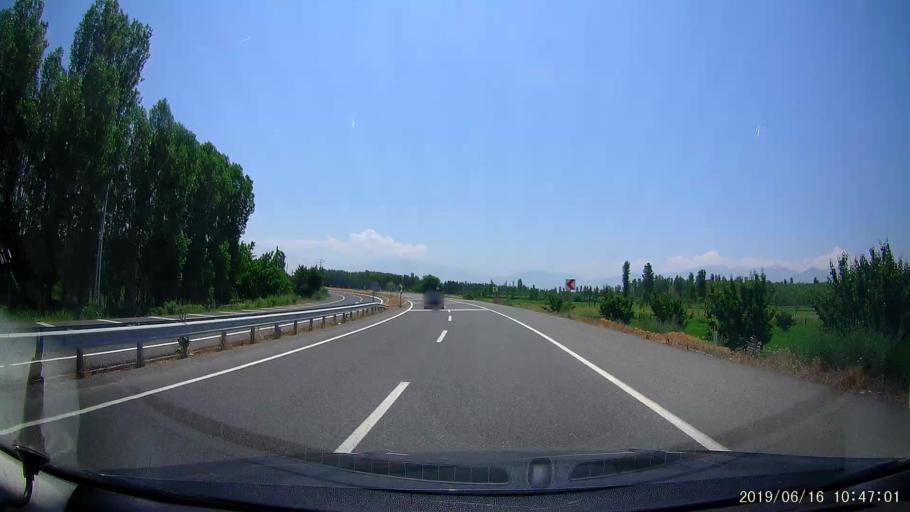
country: AM
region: Armavir
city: Shenavan
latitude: 40.0159
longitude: 43.8832
